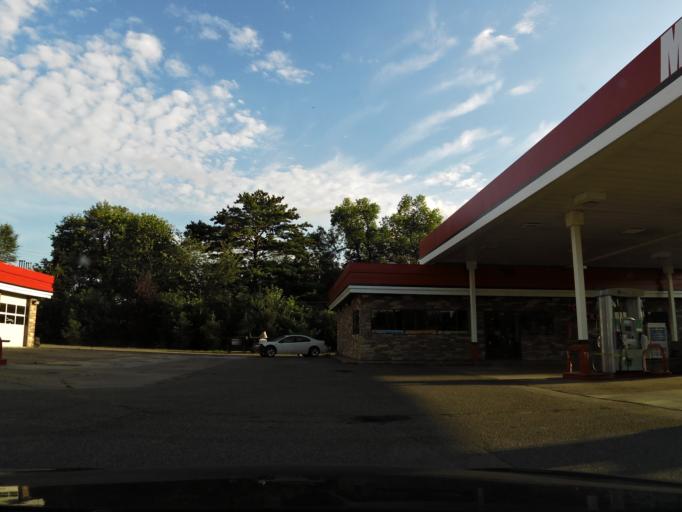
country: US
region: Minnesota
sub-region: Dakota County
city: Hastings
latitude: 44.7352
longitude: -92.8545
